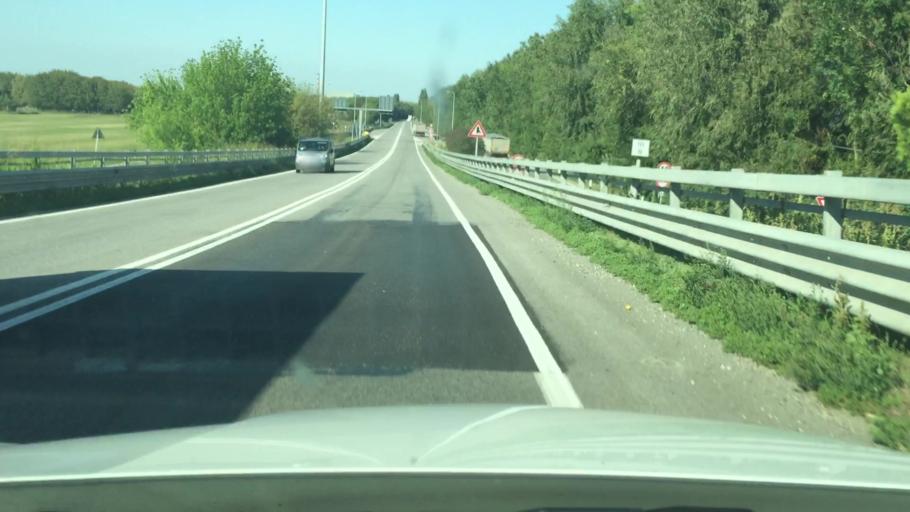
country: IT
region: Emilia-Romagna
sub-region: Provincia di Ravenna
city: Ravenna
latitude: 44.4593
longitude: 12.2089
